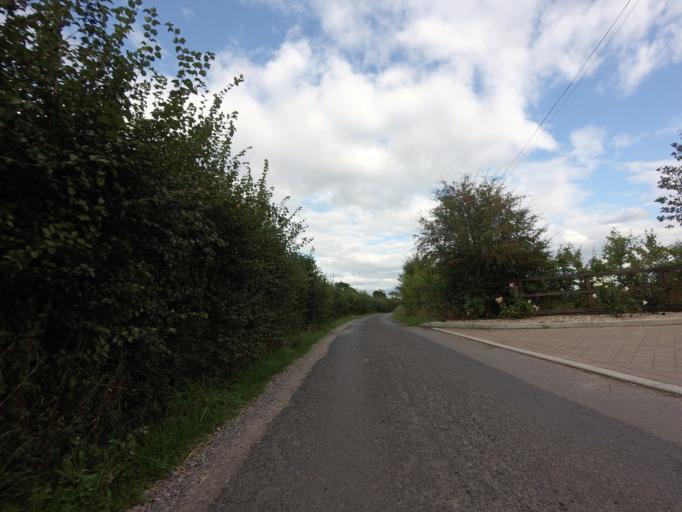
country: GB
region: England
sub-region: Kent
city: Staplehurst
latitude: 51.2079
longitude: 0.5346
